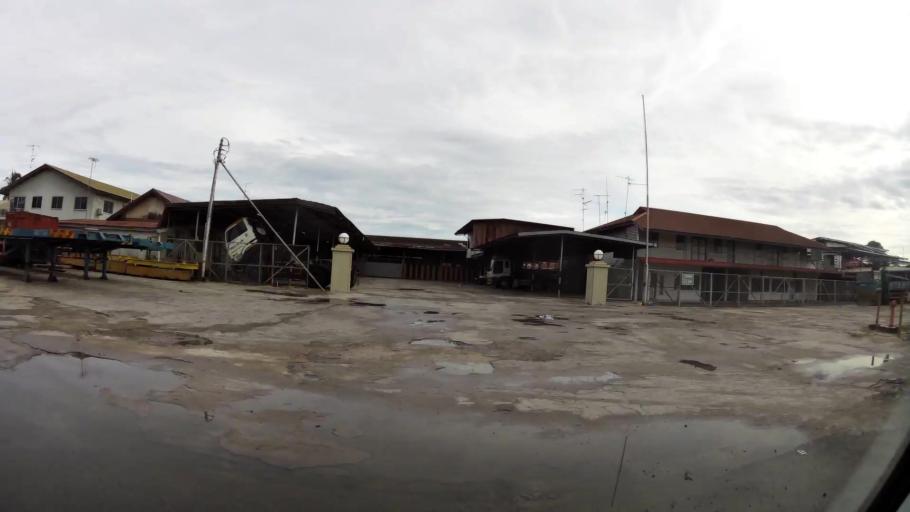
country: BN
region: Belait
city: Seria
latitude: 4.6107
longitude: 114.3385
